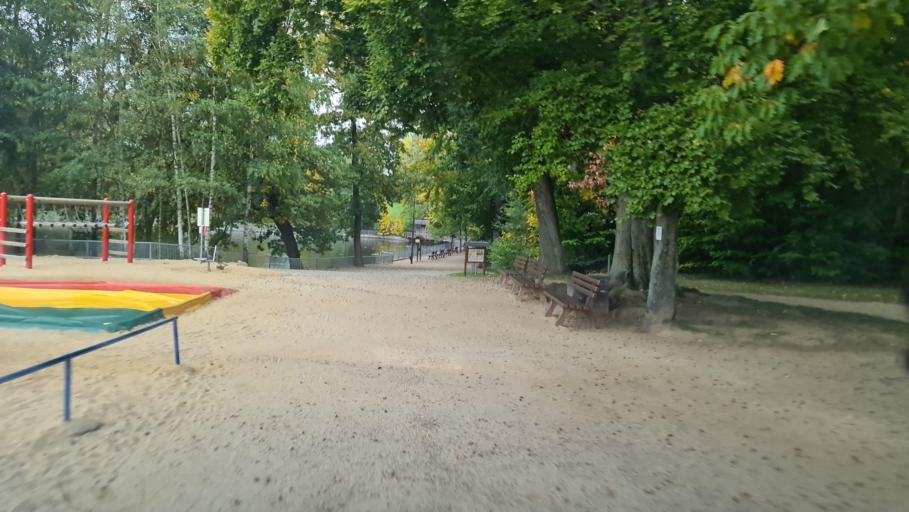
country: DE
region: Saxony
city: Hirschfeld
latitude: 50.6275
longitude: 12.4392
